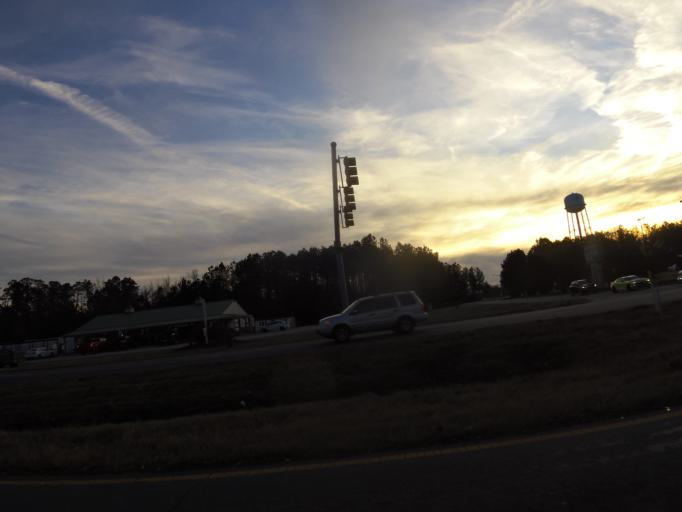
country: US
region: Virginia
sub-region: Southampton County
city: Courtland
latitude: 36.6866
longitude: -77.0228
